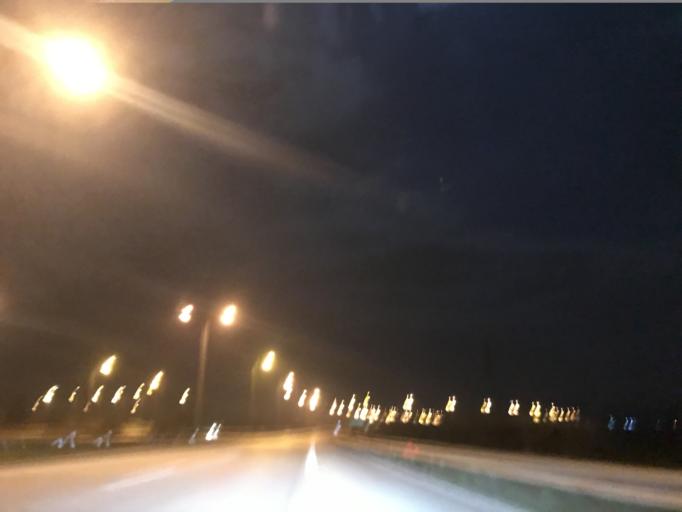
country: TR
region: Hatay
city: Mahmutlar
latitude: 36.9649
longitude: 36.1073
